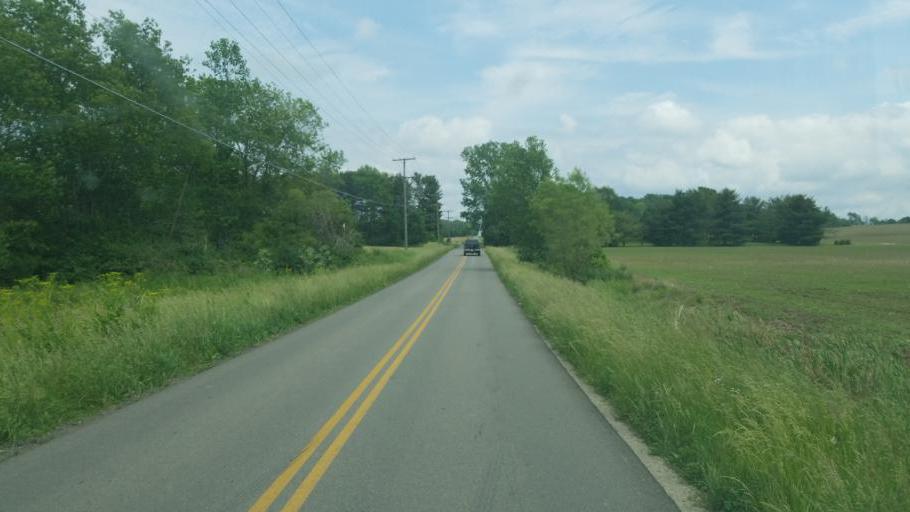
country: US
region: Ohio
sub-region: Fairfield County
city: Fairfield Beach
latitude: 39.9122
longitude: -82.4592
